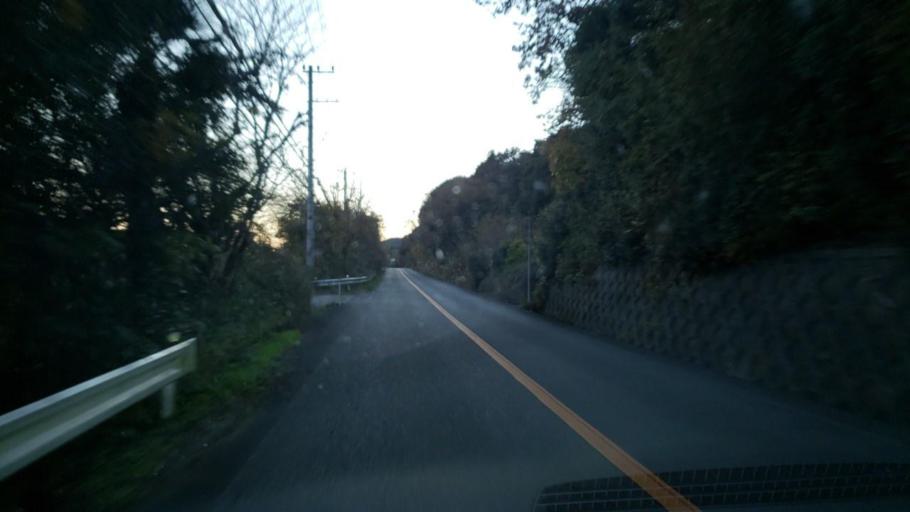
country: JP
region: Hyogo
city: Fukura
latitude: 34.2950
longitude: 134.7266
